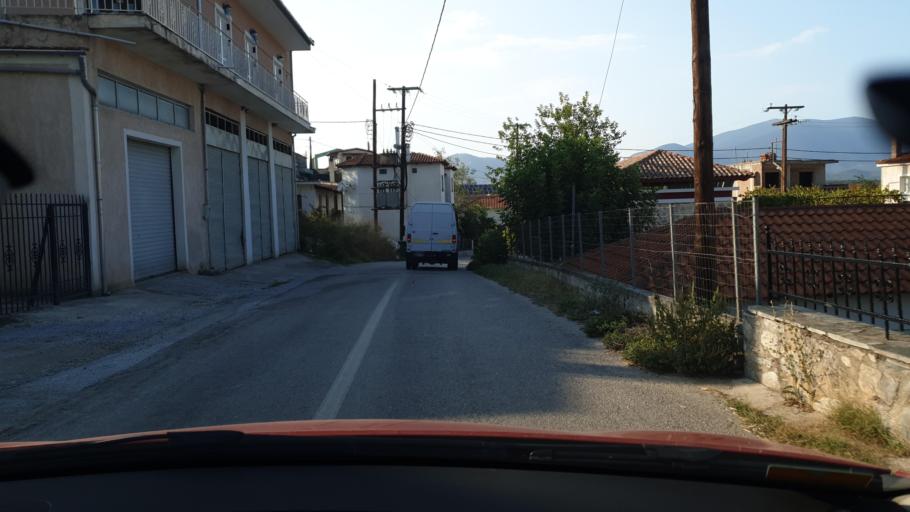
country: GR
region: Thessaly
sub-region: Nomos Magnisias
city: Pteleos
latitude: 39.0038
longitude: 22.9634
